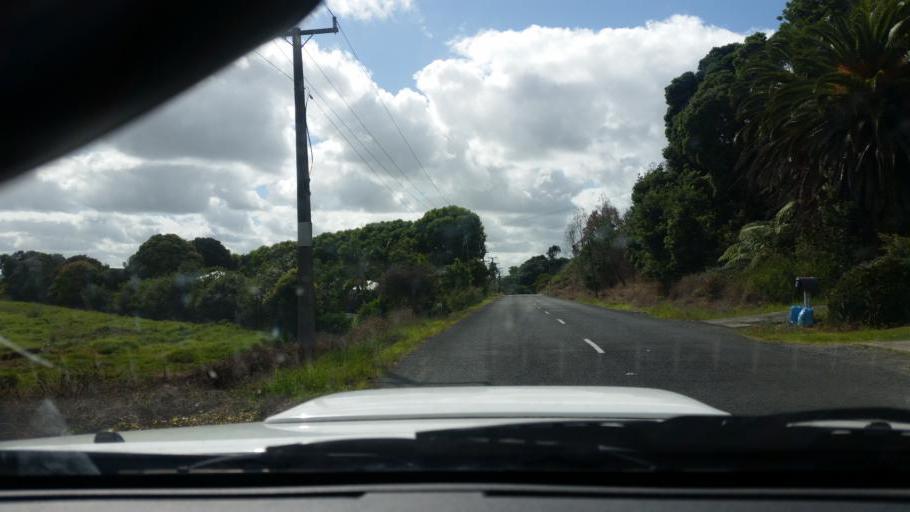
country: NZ
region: Northland
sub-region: Kaipara District
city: Dargaville
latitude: -35.9553
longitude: 173.8607
